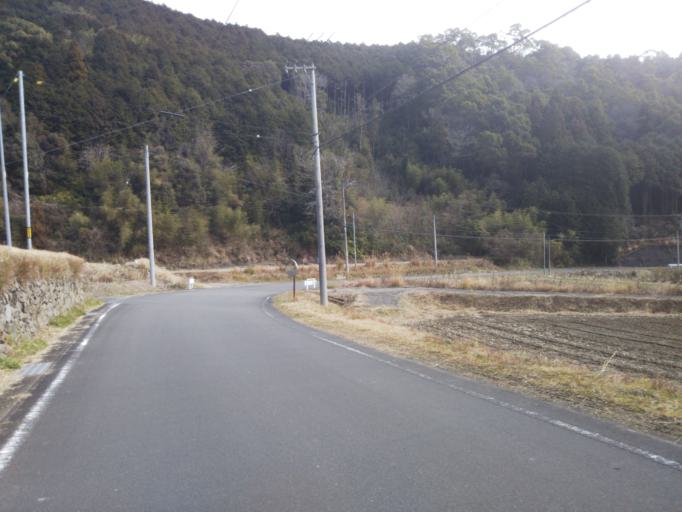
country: JP
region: Kochi
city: Nakamura
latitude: 33.0384
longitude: 132.9769
